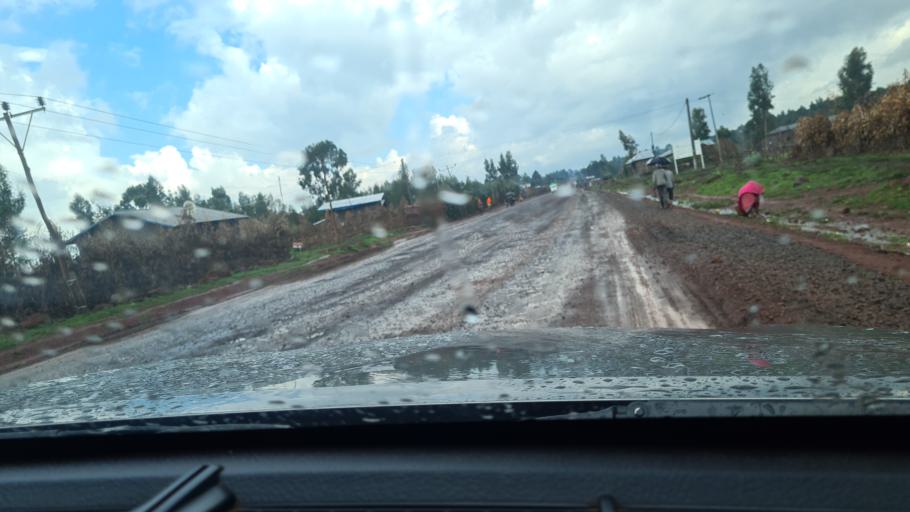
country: ET
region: Oromiya
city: Huruta
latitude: 8.0763
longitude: 39.5472
